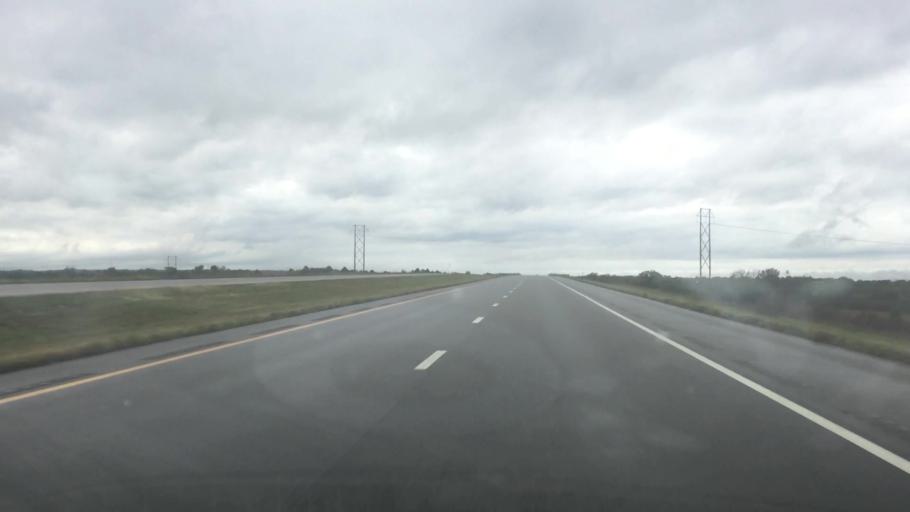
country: US
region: Kansas
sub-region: Miami County
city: Osawatomie
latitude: 38.5241
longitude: -94.9041
